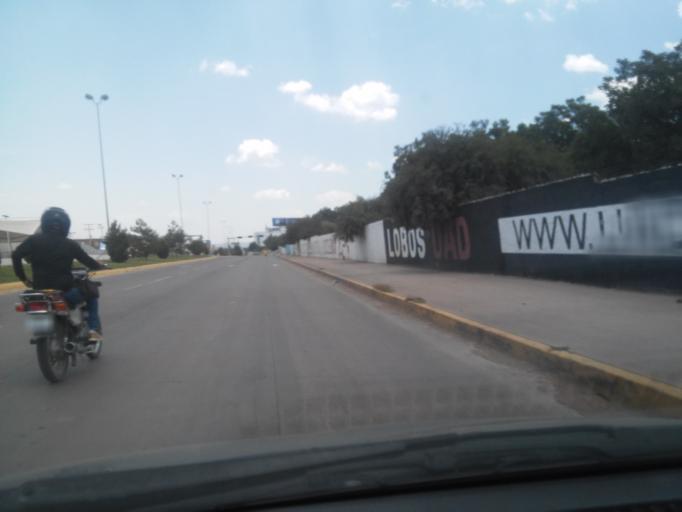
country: MX
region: Durango
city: Victoria de Durango
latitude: 24.0598
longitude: -104.6351
